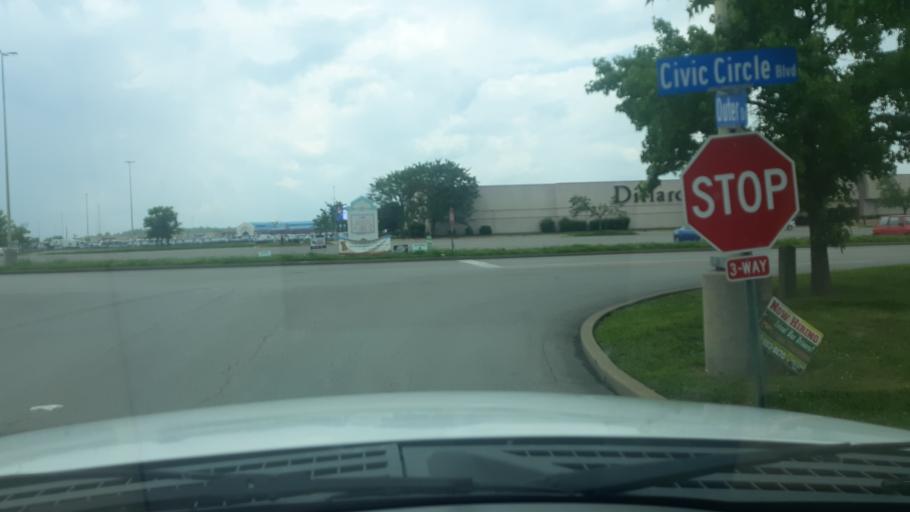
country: US
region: Illinois
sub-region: Williamson County
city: Marion
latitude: 37.7464
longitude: -88.9742
